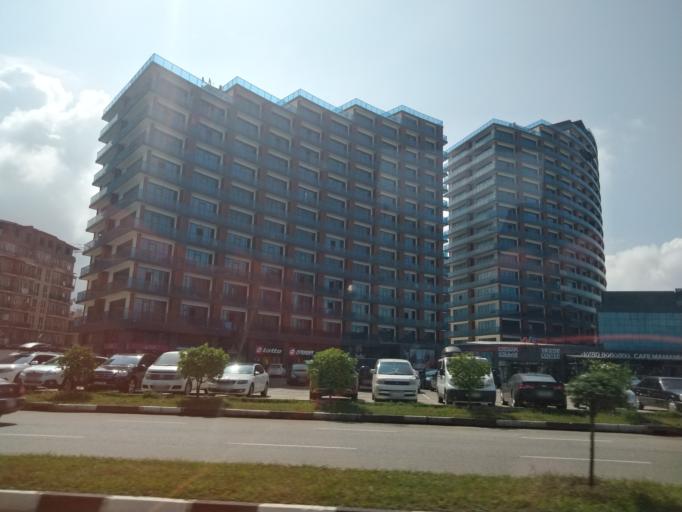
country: GE
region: Ajaria
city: Batumi
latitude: 41.6291
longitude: 41.6021
